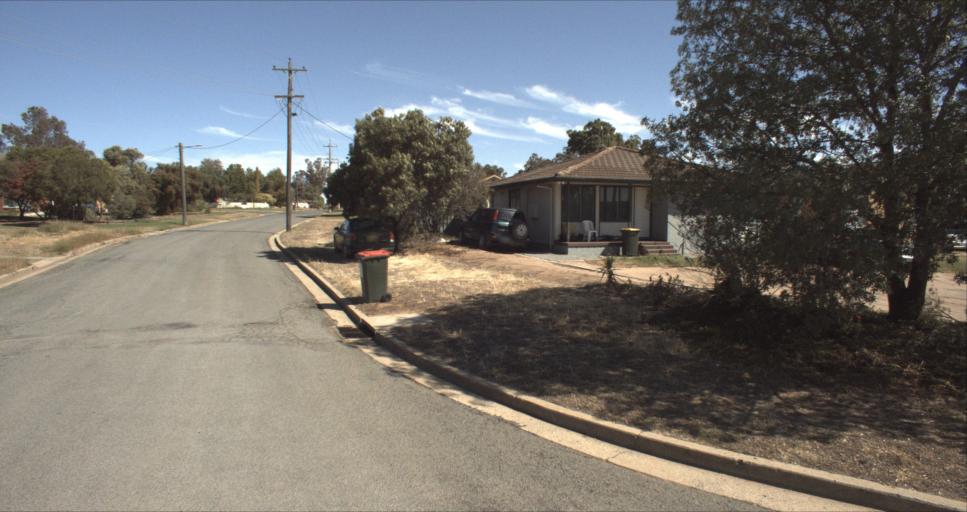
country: AU
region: New South Wales
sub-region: Leeton
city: Leeton
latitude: -34.5483
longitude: 146.3743
